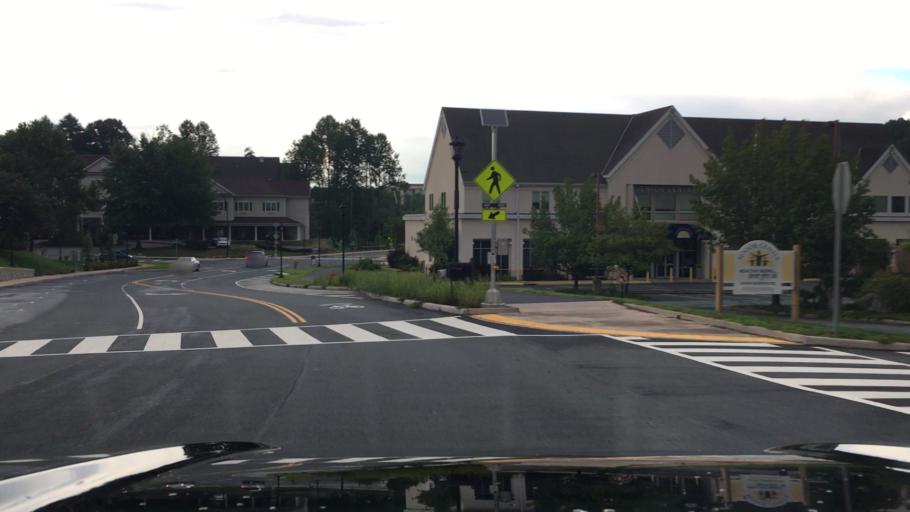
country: US
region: Virginia
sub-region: City of Charlottesville
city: Charlottesville
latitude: 38.0682
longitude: -78.4818
